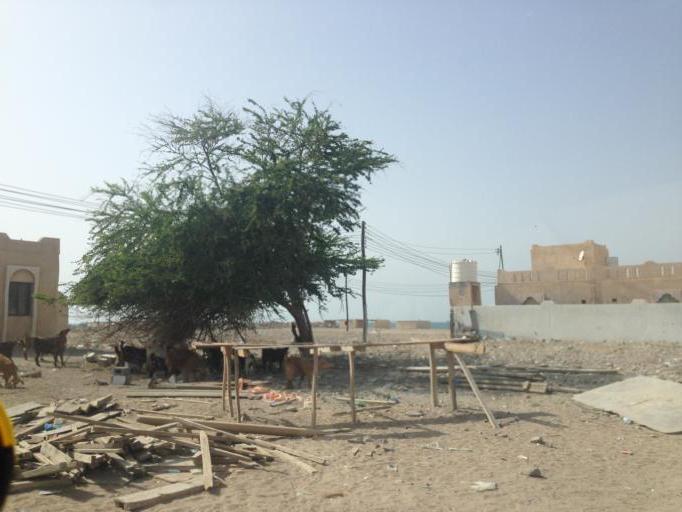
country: OM
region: Al Batinah
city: Barka'
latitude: 23.7067
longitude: 57.9246
